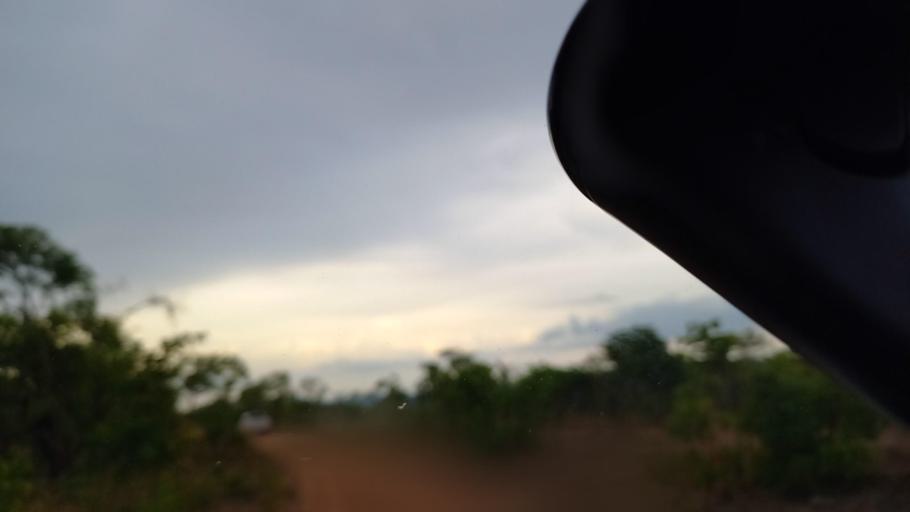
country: ZM
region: Lusaka
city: Kafue
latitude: -16.0506
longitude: 28.3339
